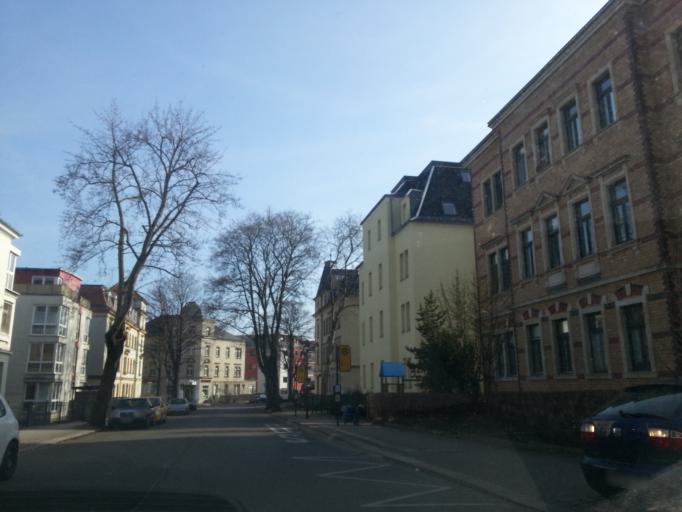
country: DE
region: Saxony
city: Radebeul
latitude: 51.0617
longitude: 13.6777
